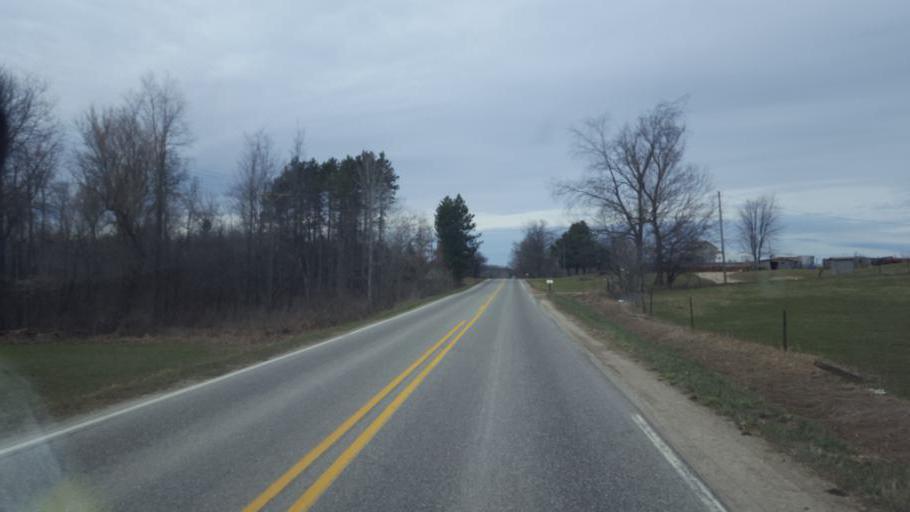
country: US
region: Michigan
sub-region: Isabella County
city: Lake Isabella
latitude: 43.5339
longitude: -85.0261
